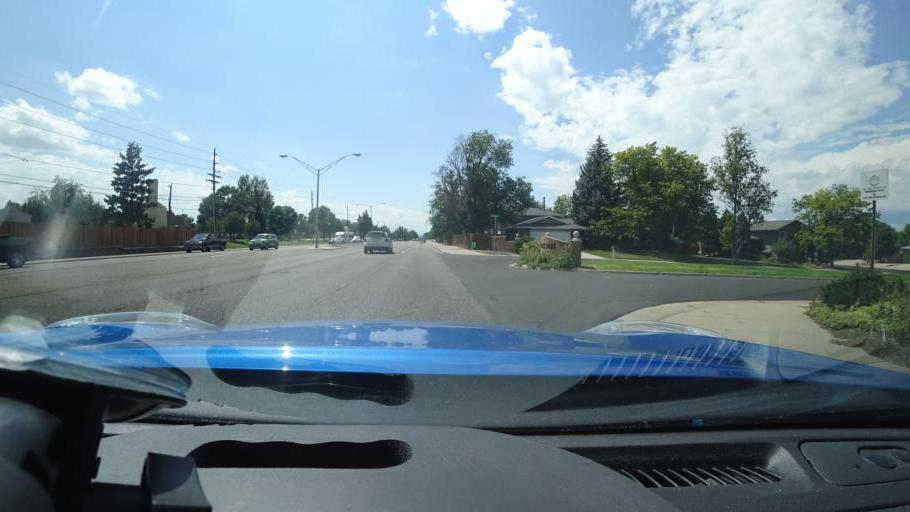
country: US
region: Colorado
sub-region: Adams County
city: Aurora
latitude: 39.7113
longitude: -104.8405
